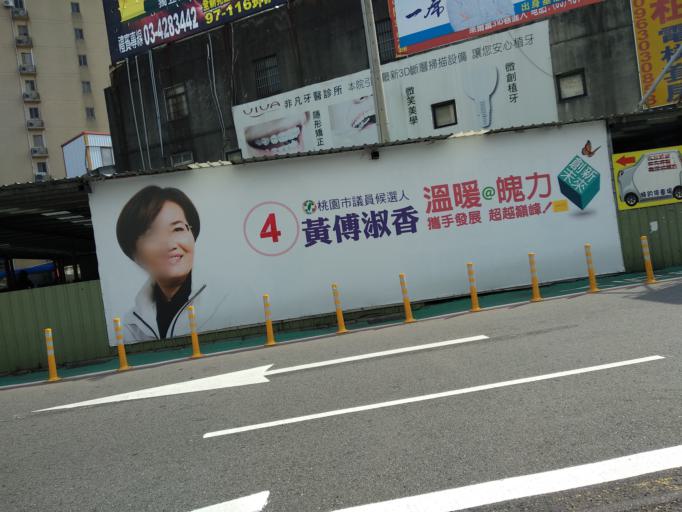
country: TW
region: Taiwan
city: Taoyuan City
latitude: 24.9520
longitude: 121.2267
